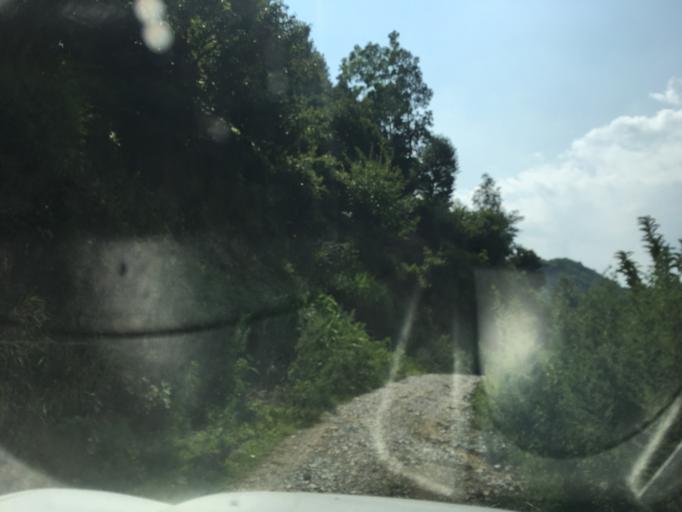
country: CN
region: Guangxi Zhuangzu Zizhiqu
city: Xinzhou
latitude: 24.9873
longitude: 105.7375
